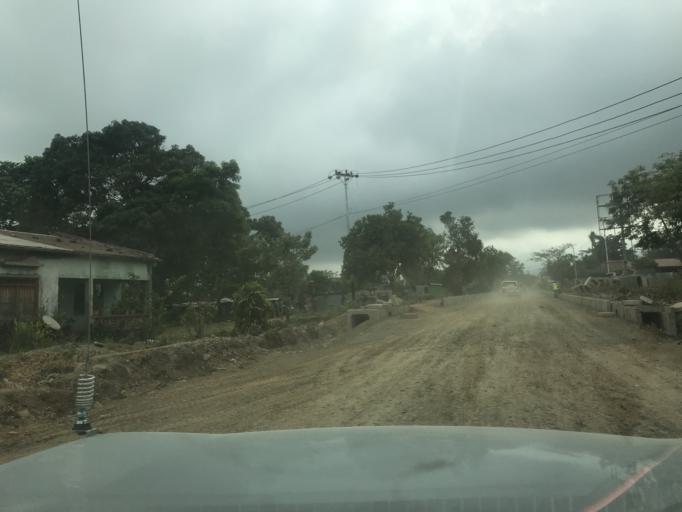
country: TL
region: Ainaro
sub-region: Ainaro
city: Ainaro
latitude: -8.9909
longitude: 125.5112
